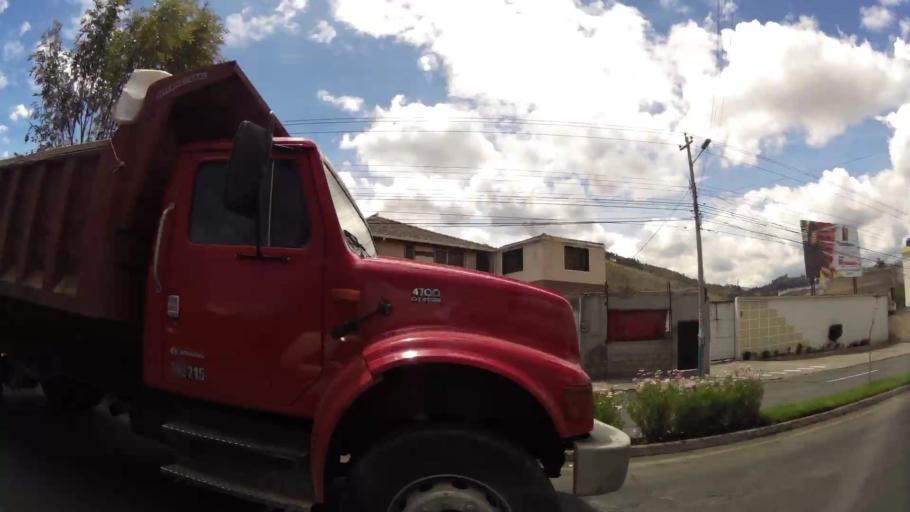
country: EC
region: Tungurahua
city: Ambato
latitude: -1.2682
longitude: -78.6378
